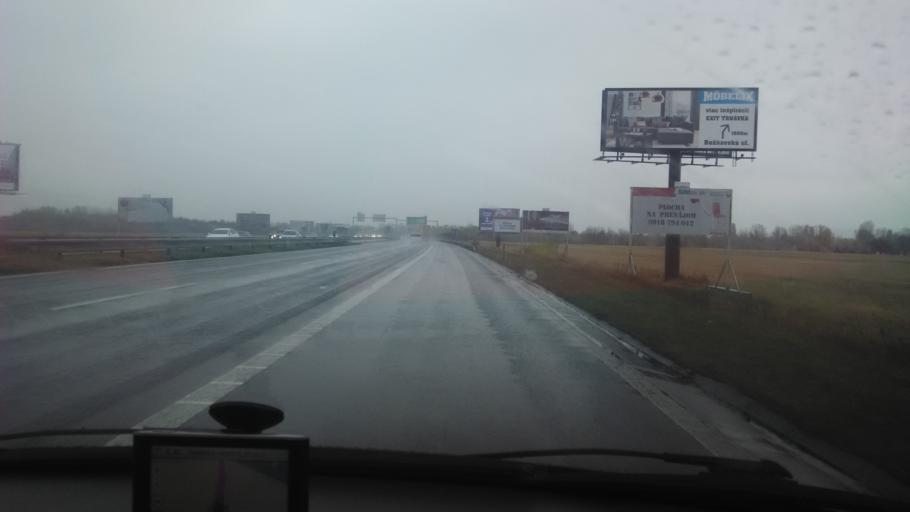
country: SK
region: Bratislavsky
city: Svaty Jur
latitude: 48.1841
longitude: 17.1986
